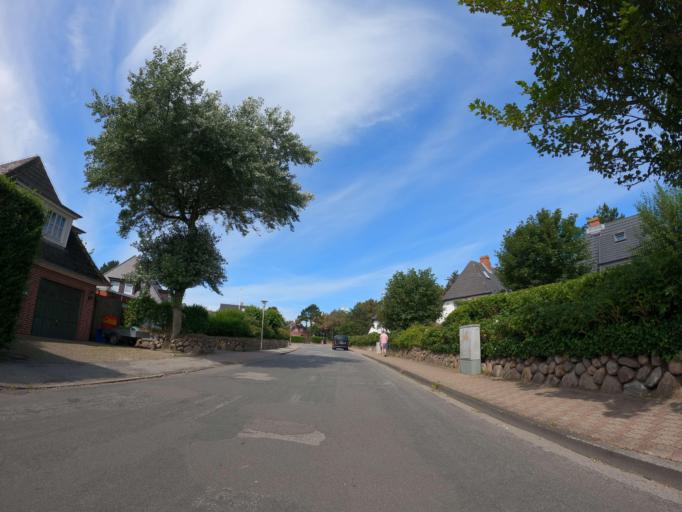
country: DE
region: Schleswig-Holstein
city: Westerland
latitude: 54.9199
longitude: 8.3140
